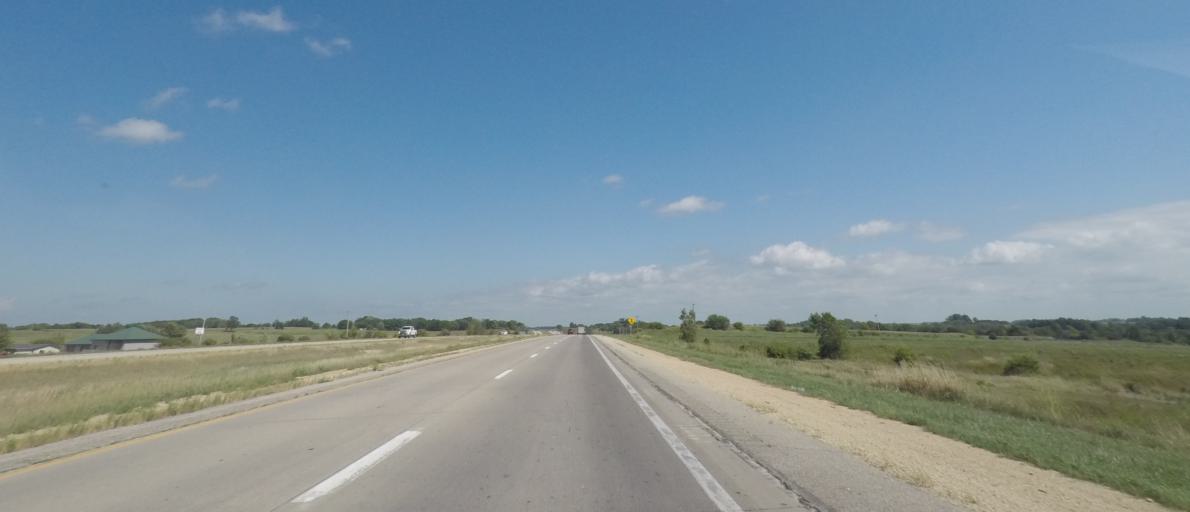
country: US
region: Iowa
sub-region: Jones County
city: Anamosa
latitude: 42.0708
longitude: -91.3348
